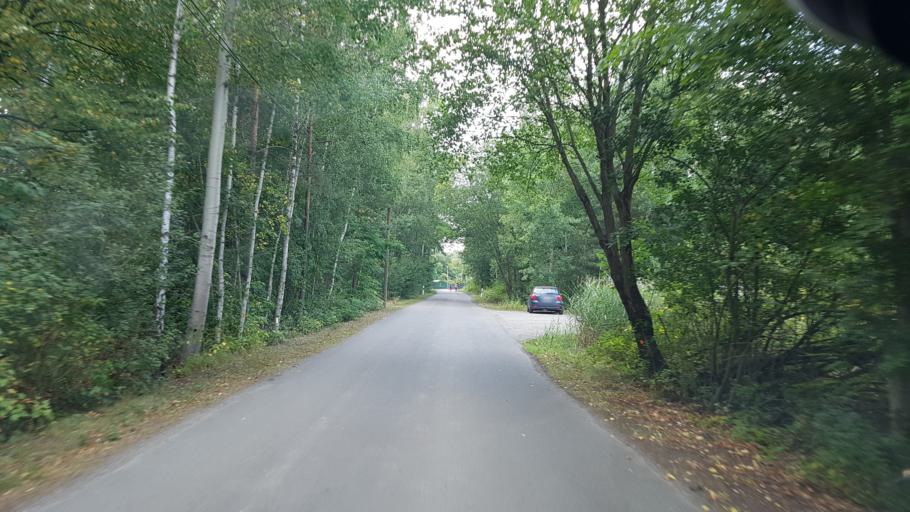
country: DE
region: Brandenburg
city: Plessa
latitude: 51.5122
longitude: 13.6722
